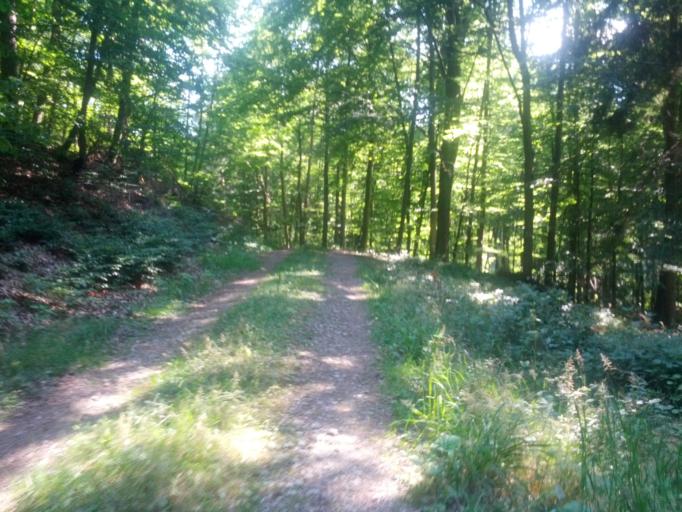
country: DE
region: Thuringia
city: Eisenach
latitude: 50.9731
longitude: 10.2809
